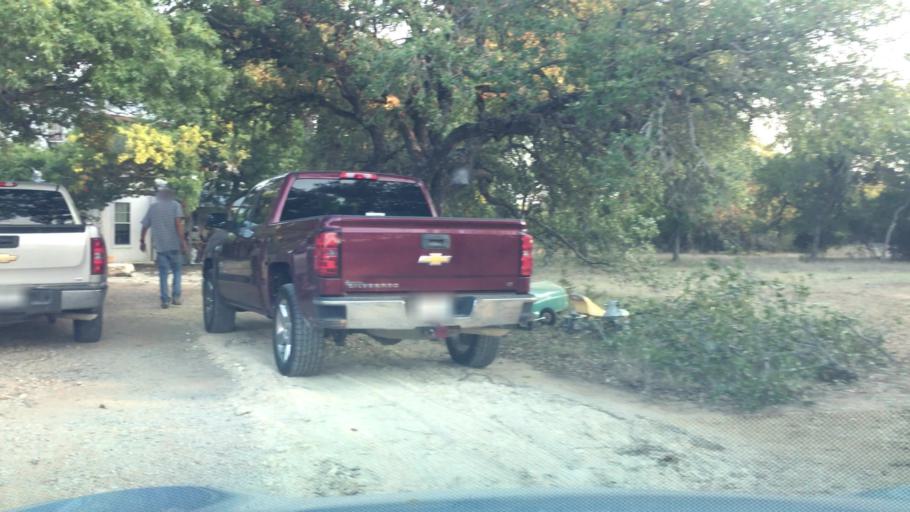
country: US
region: Texas
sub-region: Hays County
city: Dripping Springs
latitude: 30.1522
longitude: -98.0255
